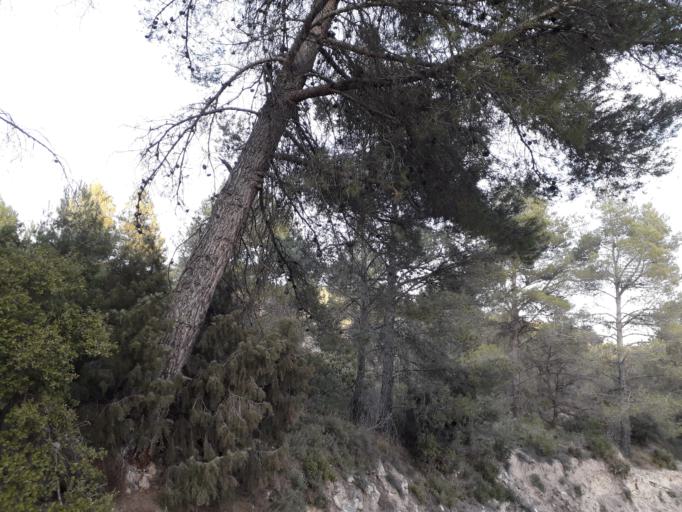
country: ES
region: Catalonia
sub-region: Provincia de Barcelona
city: Sant Marti de Tous
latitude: 41.5635
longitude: 1.4764
